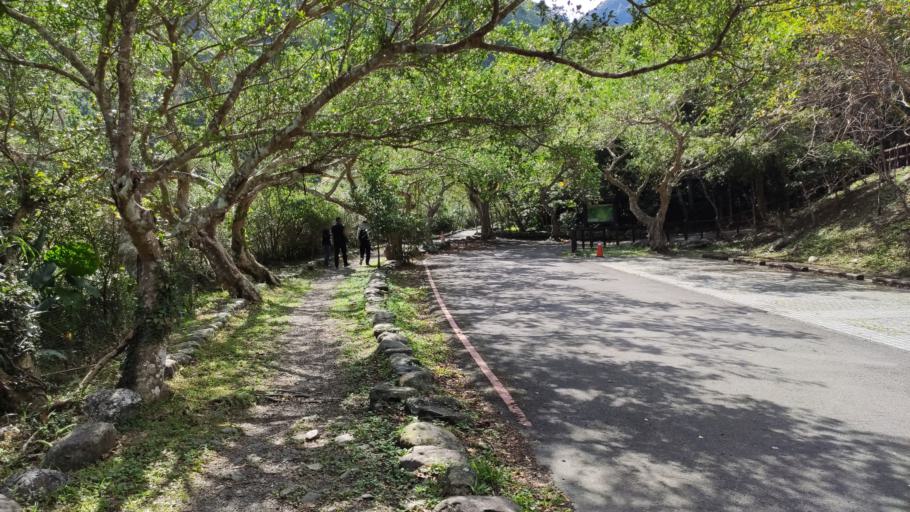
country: TW
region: Taiwan
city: Daxi
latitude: 24.8330
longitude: 121.4461
